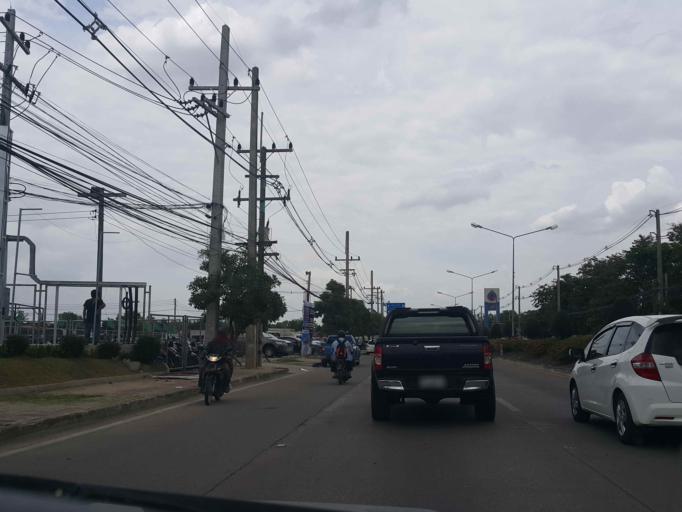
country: TH
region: Chiang Mai
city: Hang Dong
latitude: 18.7290
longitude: 98.9497
